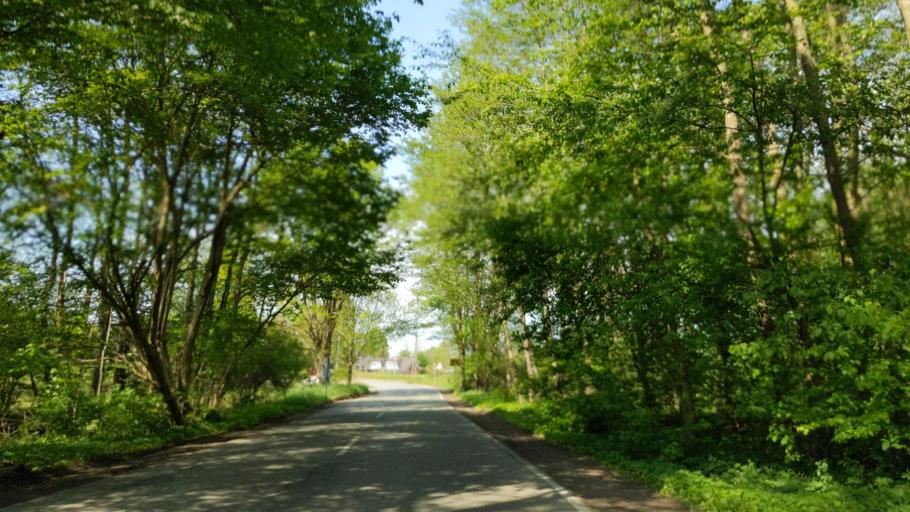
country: DE
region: Mecklenburg-Vorpommern
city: Selmsdorf
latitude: 53.8755
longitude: 10.8191
